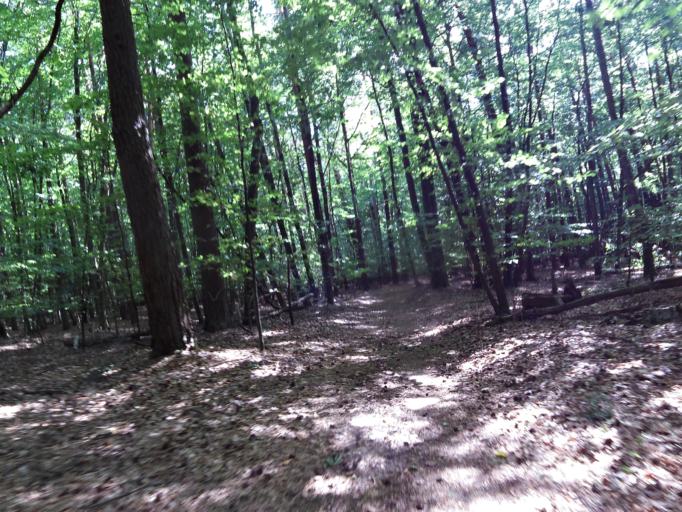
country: DE
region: Bavaria
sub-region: Regierungsbezirk Unterfranken
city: Theilheim
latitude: 49.7460
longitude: 10.0172
